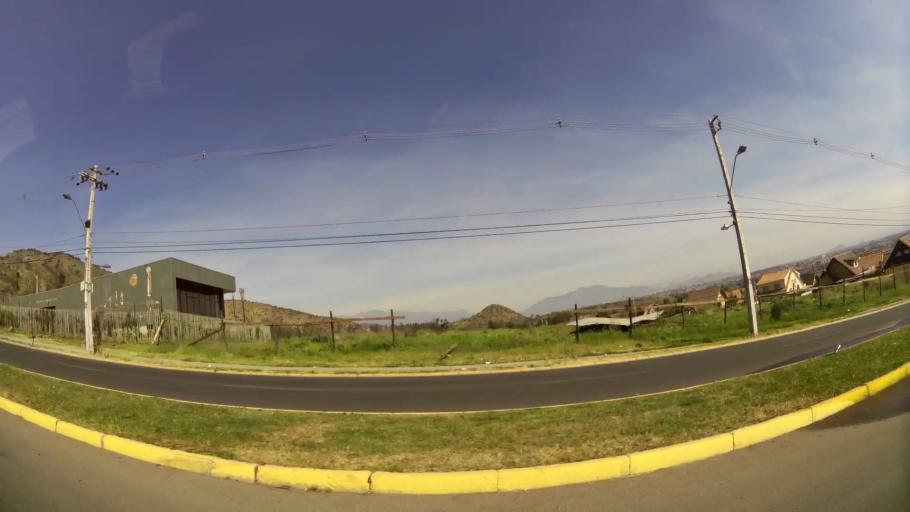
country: CL
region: Santiago Metropolitan
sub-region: Provincia de Cordillera
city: Puente Alto
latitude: -33.5357
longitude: -70.5449
